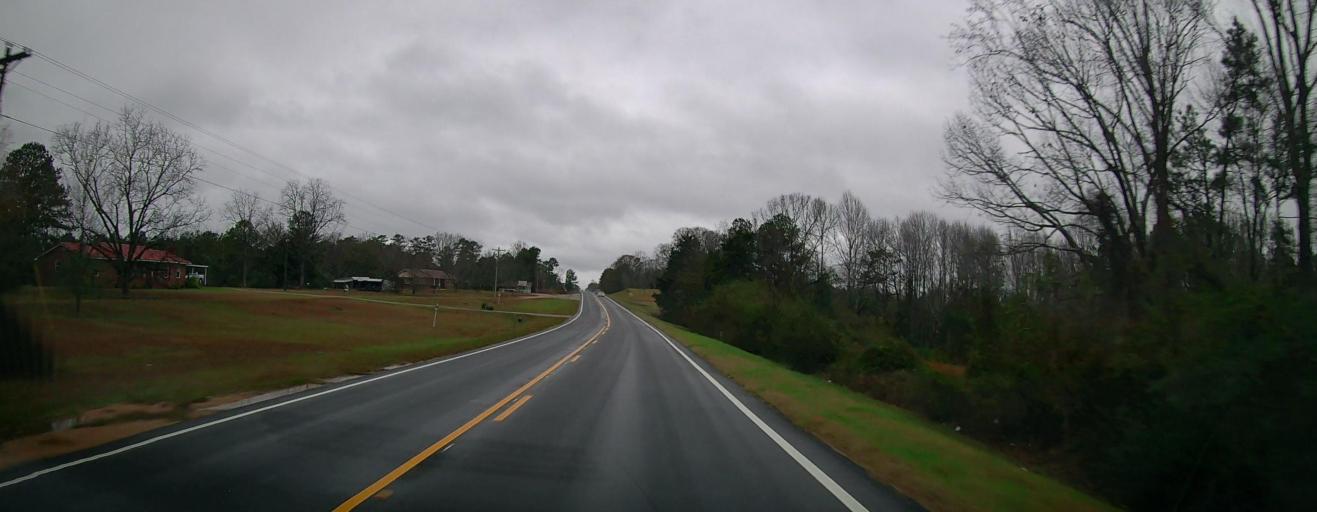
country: US
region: Alabama
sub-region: Chilton County
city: Thorsby
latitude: 32.7995
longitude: -86.9117
